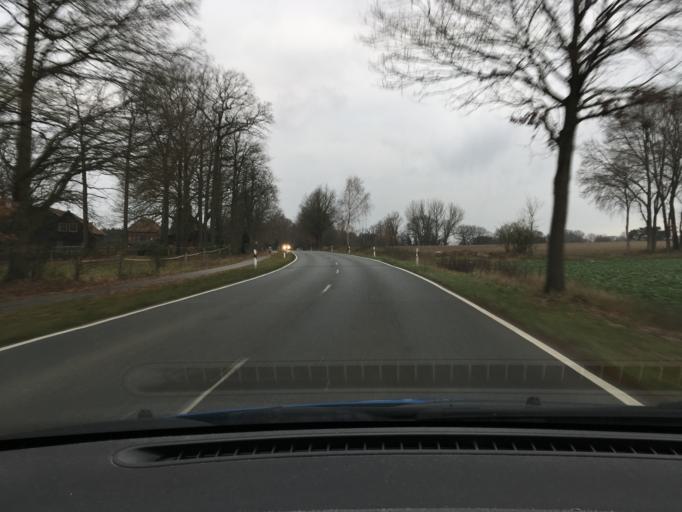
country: DE
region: Lower Saxony
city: Bad Fallingbostel
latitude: 52.8950
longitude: 9.7524
